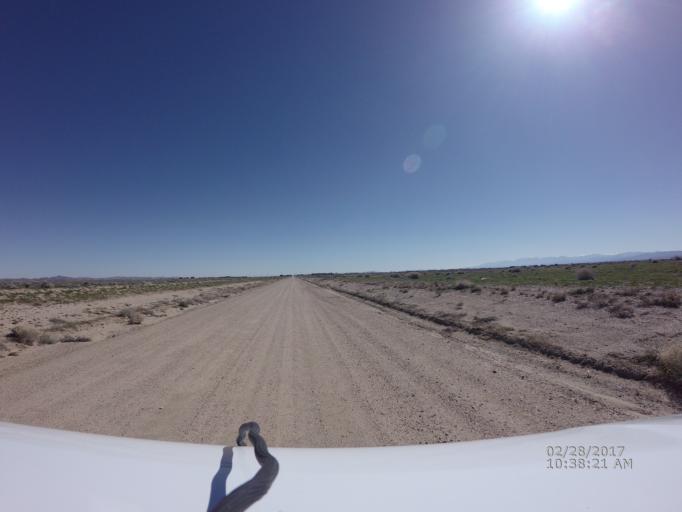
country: US
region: California
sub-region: Kern County
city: Rosamond
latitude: 34.7910
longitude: -118.3046
